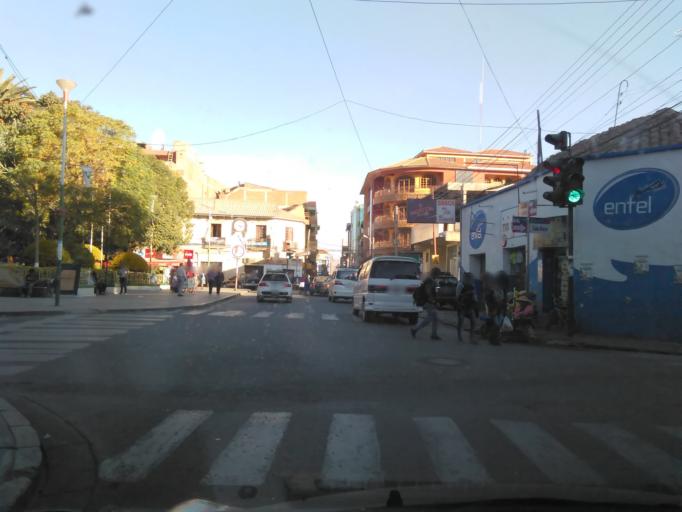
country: BO
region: Cochabamba
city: Punata
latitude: -17.5450
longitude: -65.8368
